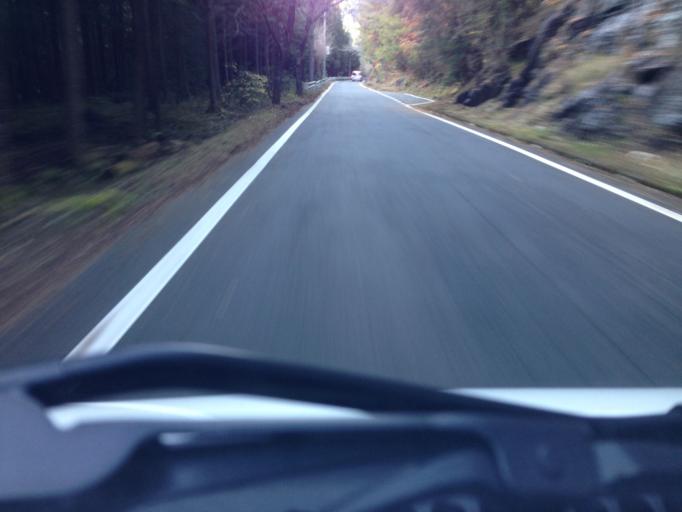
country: JP
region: Gifu
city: Mitake
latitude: 35.6072
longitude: 137.1923
